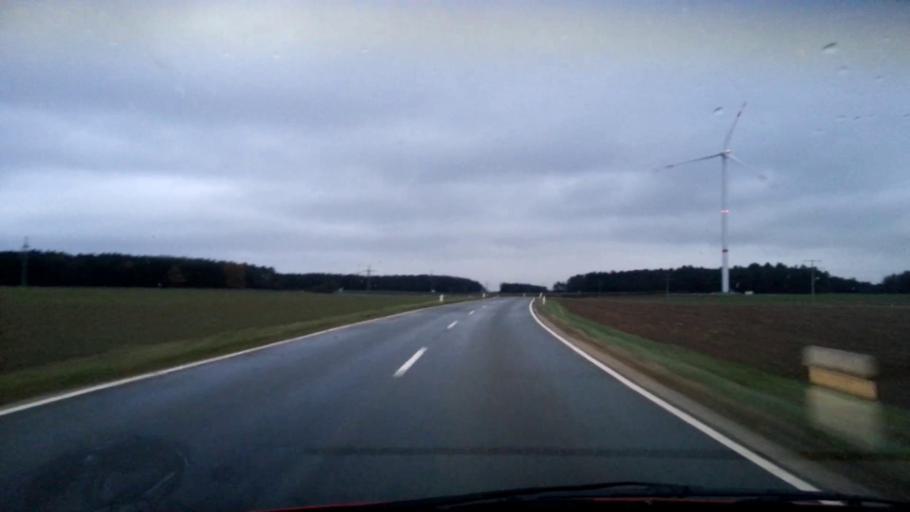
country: DE
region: Bavaria
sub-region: Upper Franconia
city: Poxdorf
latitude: 49.9814
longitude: 11.1126
